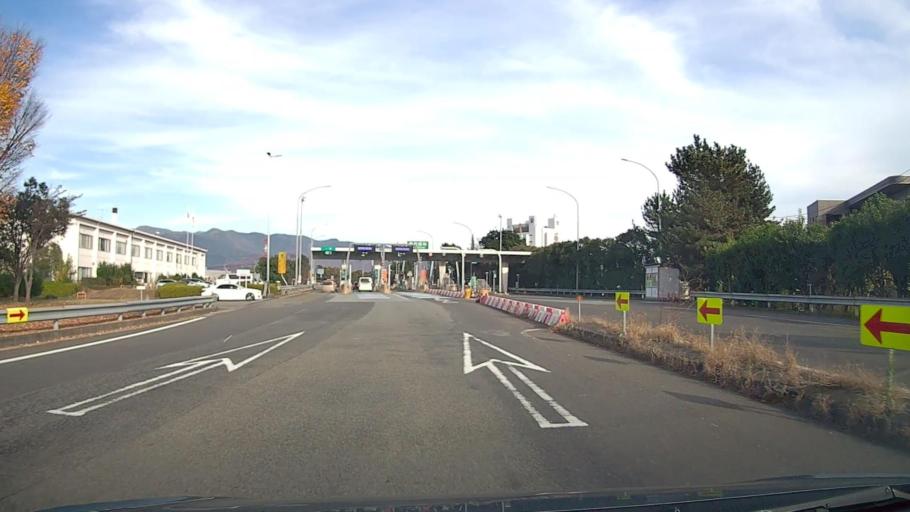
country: JP
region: Yamanashi
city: Kofu-shi
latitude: 35.6436
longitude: 138.5388
